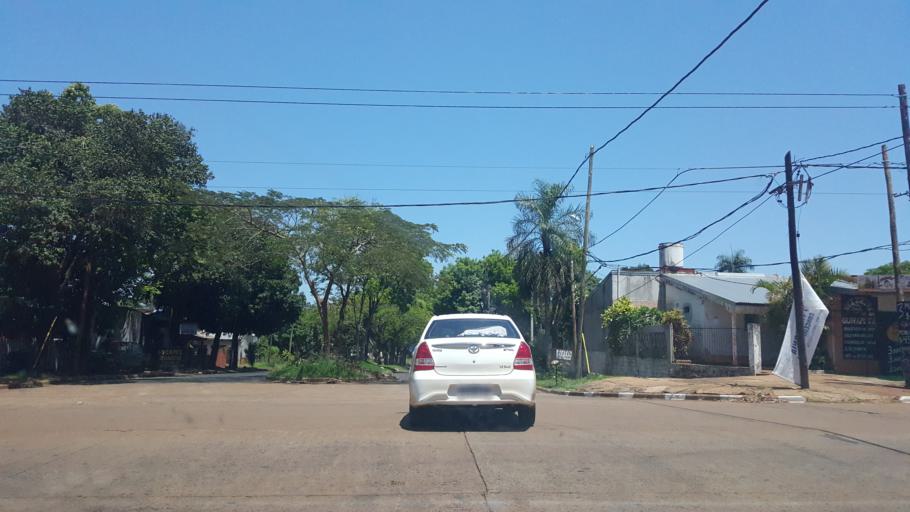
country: AR
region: Misiones
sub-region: Departamento de Capital
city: Posadas
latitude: -27.3717
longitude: -55.9210
